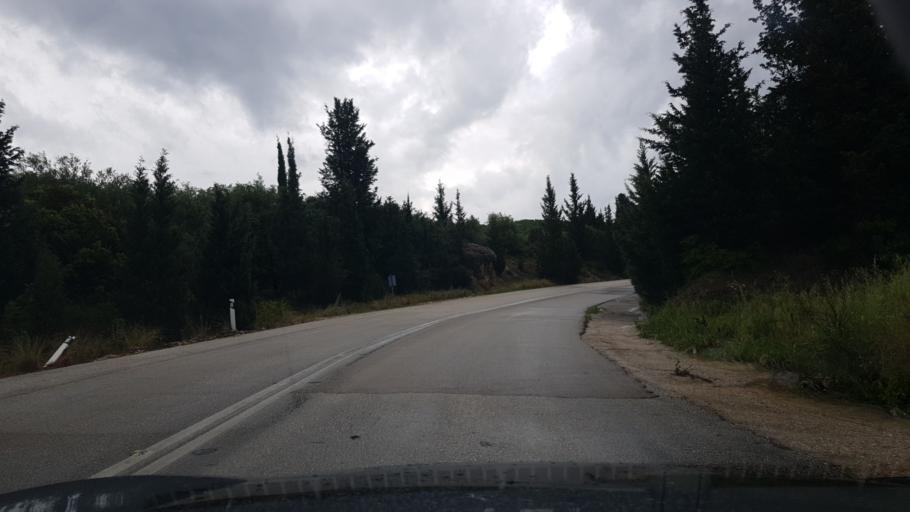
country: GR
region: Ionian Islands
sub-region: Lefkada
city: Nidri
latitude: 38.6352
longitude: 20.6296
